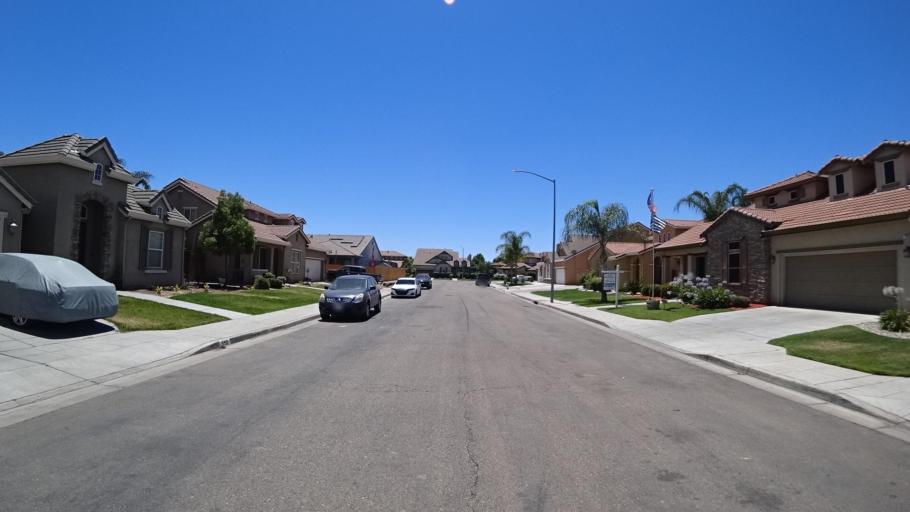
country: US
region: California
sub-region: Fresno County
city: Sunnyside
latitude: 36.7278
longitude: -119.6713
